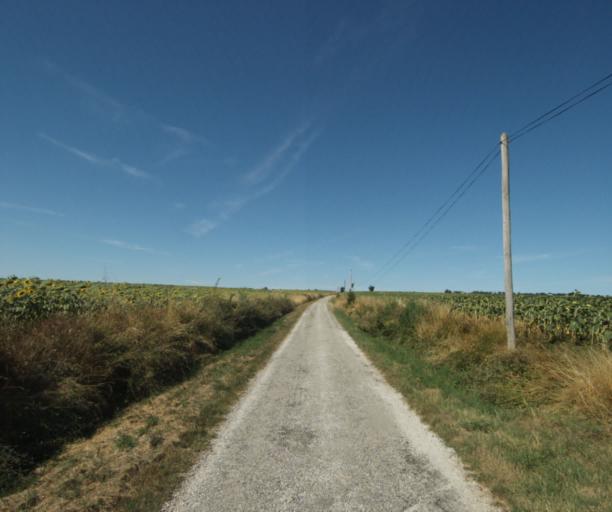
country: FR
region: Midi-Pyrenees
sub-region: Departement de la Haute-Garonne
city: Saint-Felix-Lauragais
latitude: 43.5042
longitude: 1.9026
